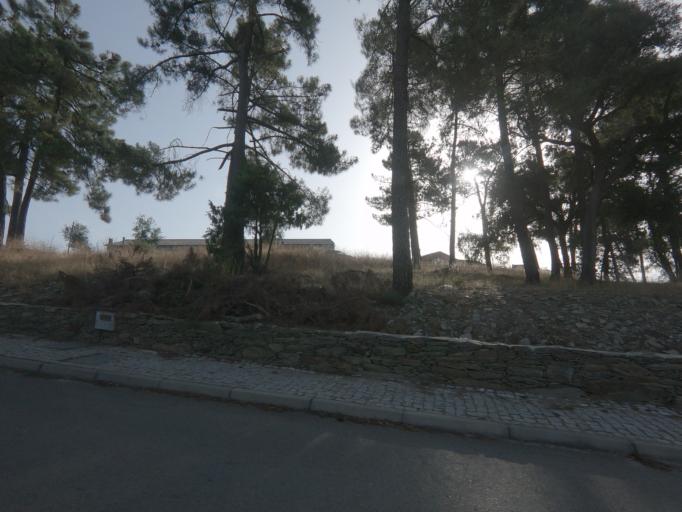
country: PT
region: Viseu
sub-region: Sao Joao da Pesqueira
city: Sao Joao da Pesqueira
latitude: 41.2295
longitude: -7.4690
